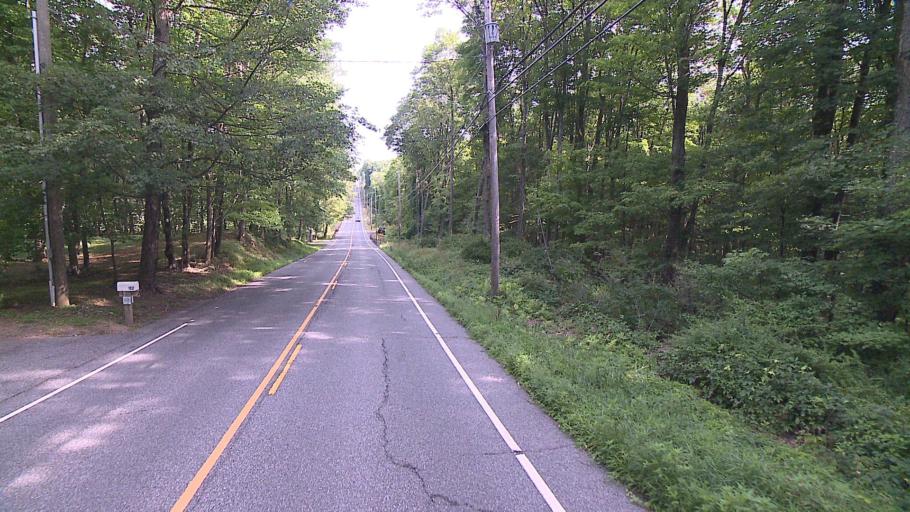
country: US
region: Connecticut
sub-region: Fairfield County
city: Sherman
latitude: 41.5516
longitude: -73.5040
